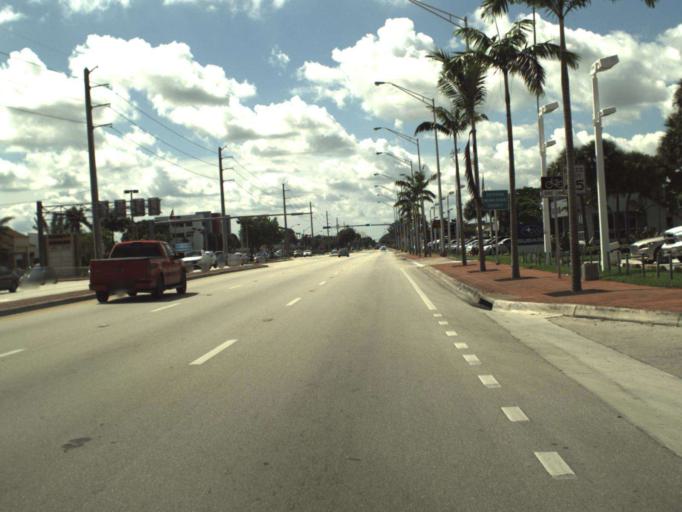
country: US
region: Florida
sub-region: Miami-Dade County
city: Andover
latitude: 25.9721
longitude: -80.2062
